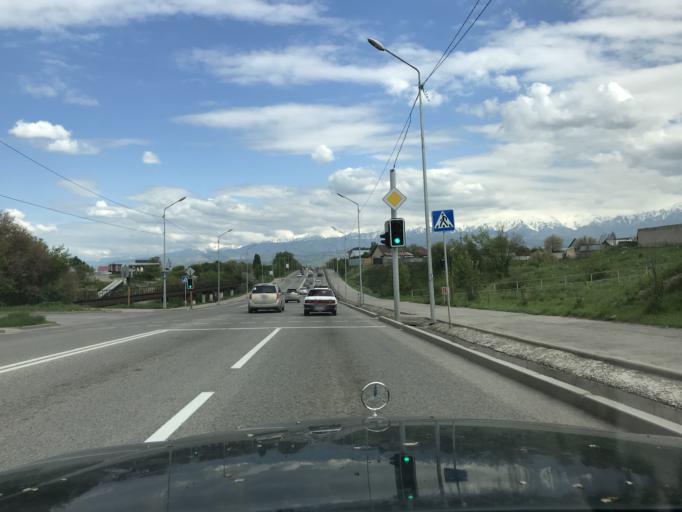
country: KZ
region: Almaty Oblysy
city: Burunday
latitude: 43.3070
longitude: 76.8786
